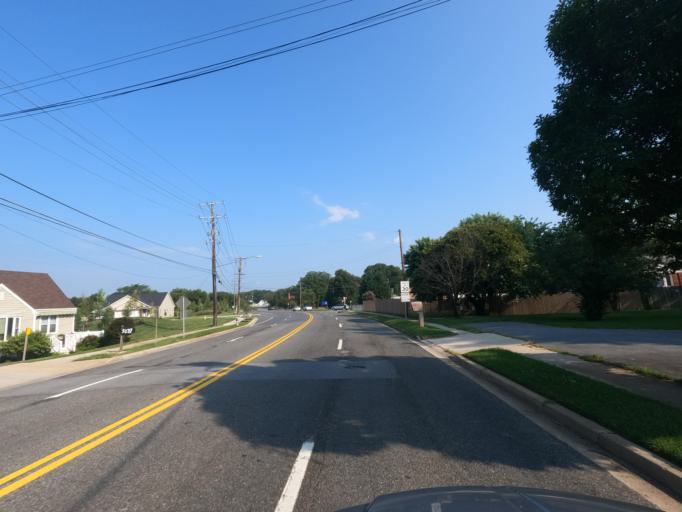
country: US
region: Maryland
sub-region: Prince George's County
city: Temple Hills
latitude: 38.8152
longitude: -76.9463
